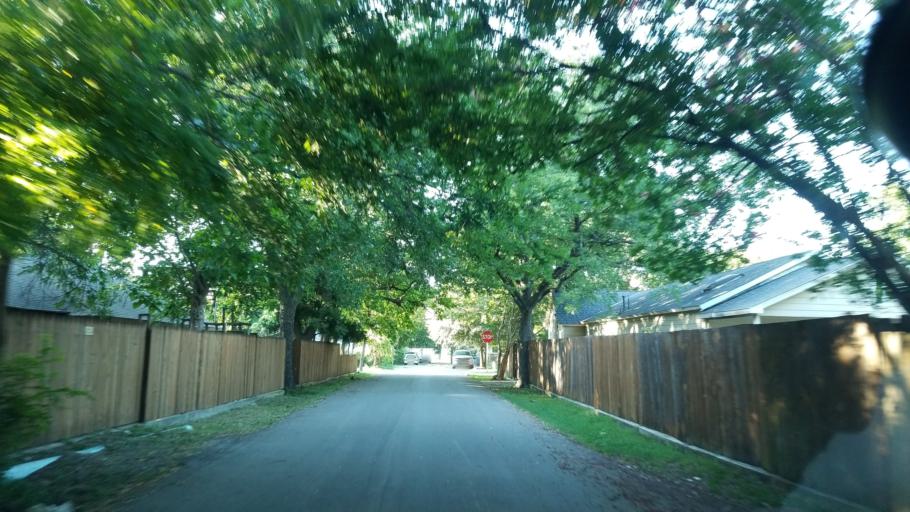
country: US
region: Texas
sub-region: Dallas County
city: Balch Springs
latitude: 32.7750
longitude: -96.6987
